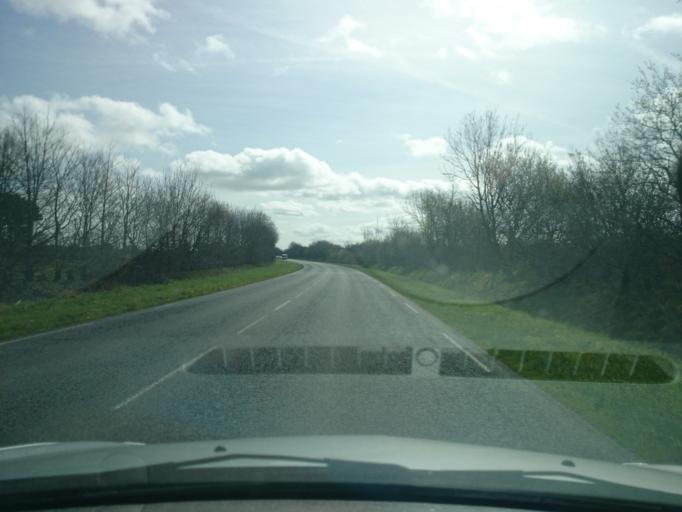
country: FR
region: Brittany
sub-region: Departement du Finistere
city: Gouesnou
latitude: 48.4379
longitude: -4.4527
